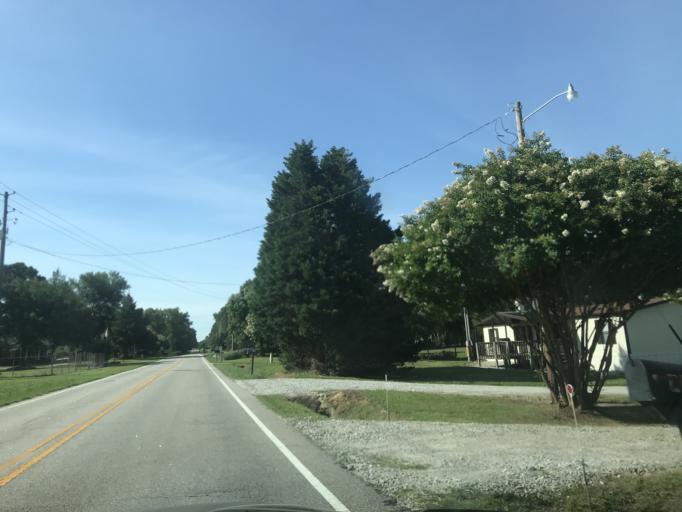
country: US
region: North Carolina
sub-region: Johnston County
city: Clayton
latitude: 35.6409
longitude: -78.5381
